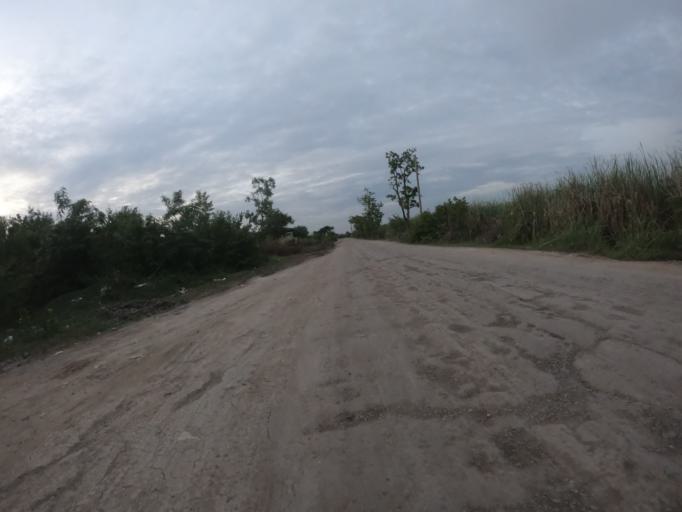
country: TH
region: Pathum Thani
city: Ban Lam Luk Ka
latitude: 14.0093
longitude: 100.8007
